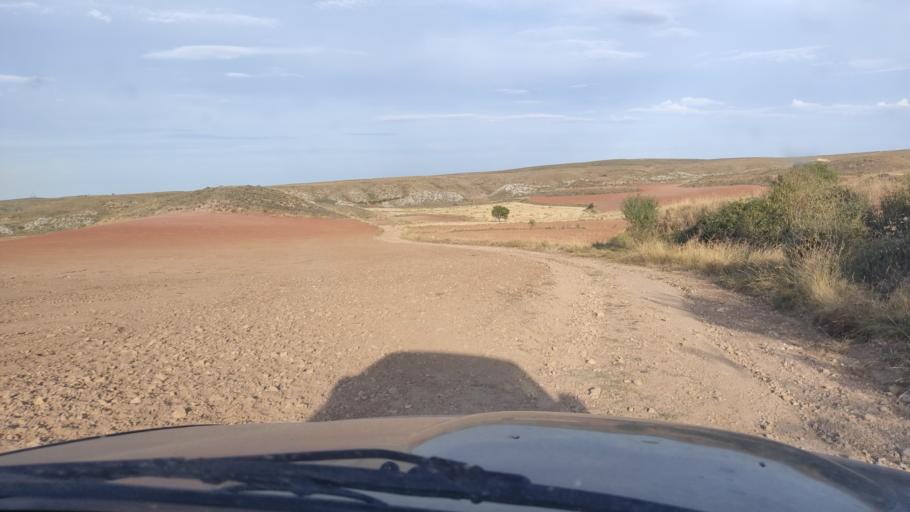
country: ES
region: Aragon
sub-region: Provincia de Teruel
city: Monforte de Moyuela
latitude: 41.0481
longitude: -0.9720
